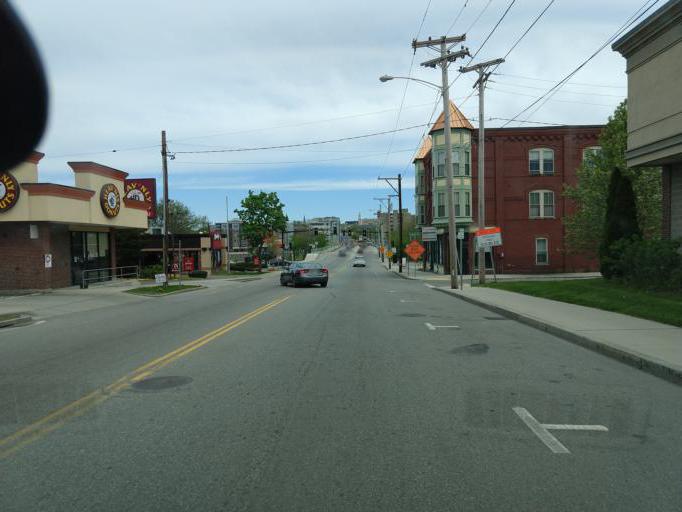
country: US
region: Massachusetts
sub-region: Essex County
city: Haverhill
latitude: 42.7714
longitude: -71.0757
